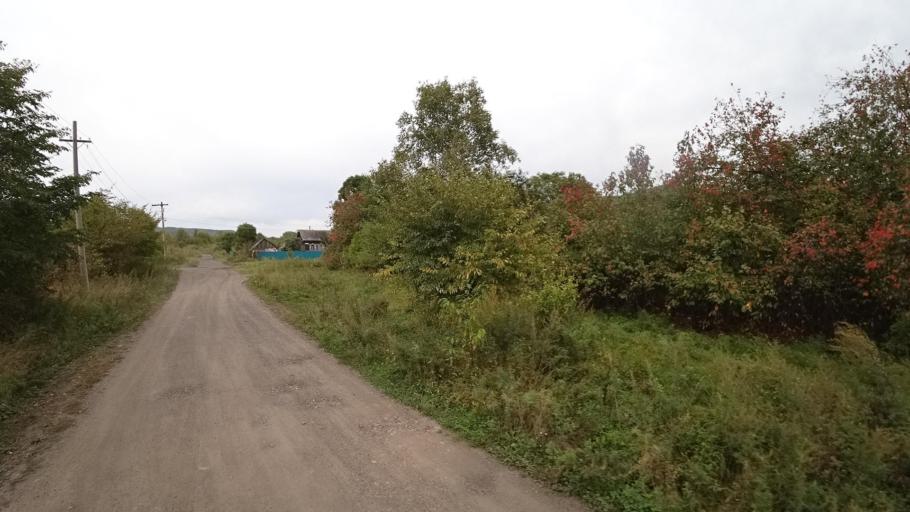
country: RU
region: Jewish Autonomous Oblast
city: Khingansk
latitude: 49.0403
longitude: 131.0497
